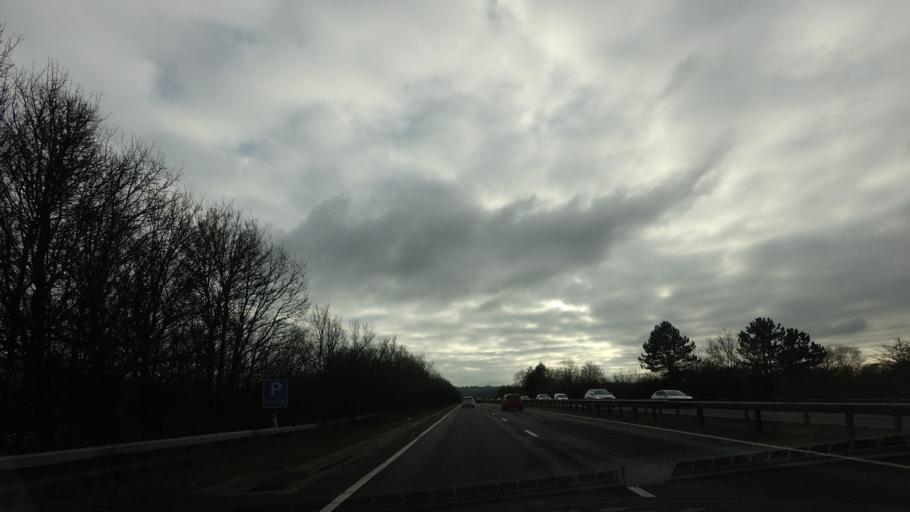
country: GB
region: England
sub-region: Kent
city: Tonbridge
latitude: 51.1958
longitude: 0.2324
